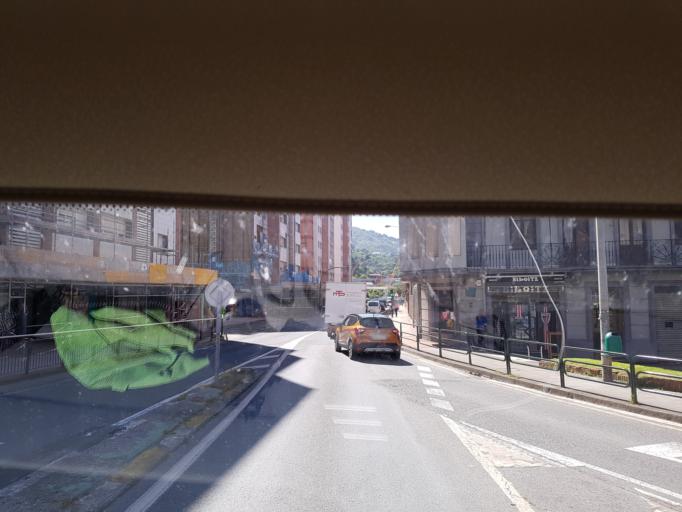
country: ES
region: Basque Country
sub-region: Bizkaia
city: Barakaldo
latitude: 43.2830
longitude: -2.9956
